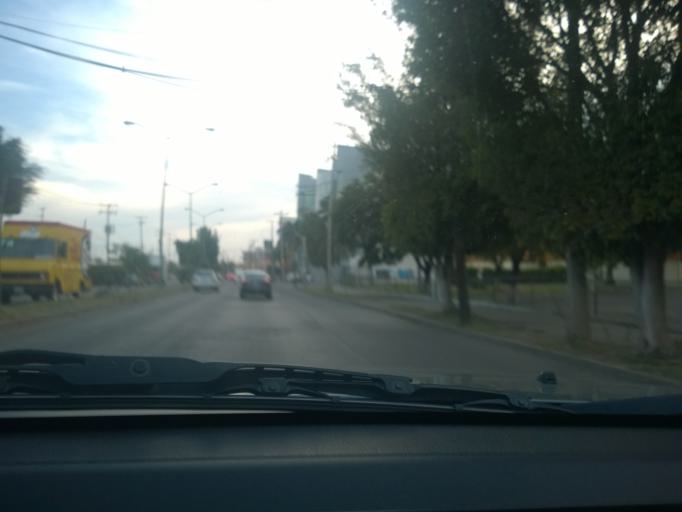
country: MX
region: Guanajuato
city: Leon
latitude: 21.1429
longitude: -101.6593
